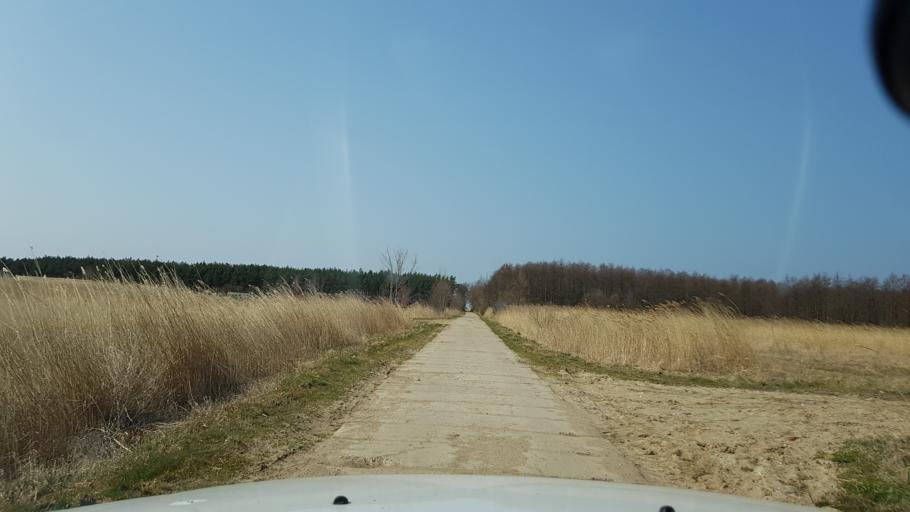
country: PL
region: West Pomeranian Voivodeship
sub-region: Powiat slawienski
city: Darlowo
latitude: 54.4626
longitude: 16.4172
